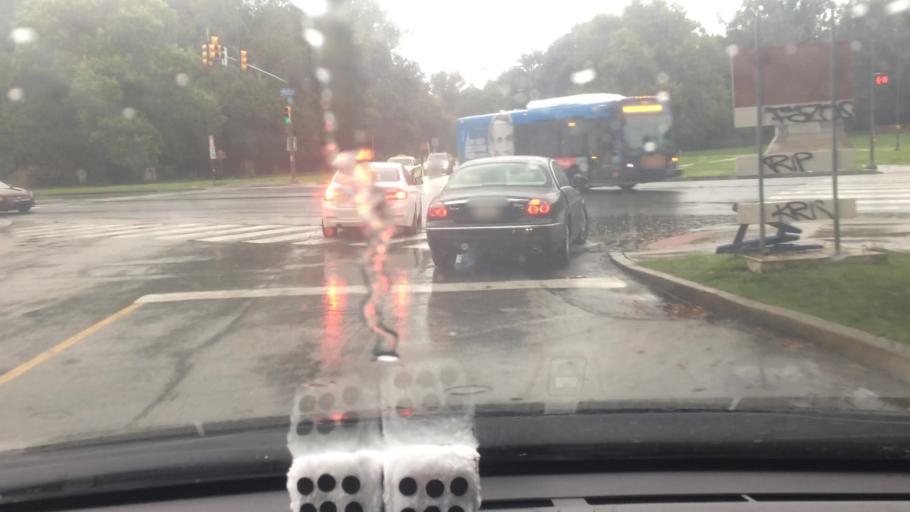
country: US
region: Pennsylvania
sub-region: Philadelphia County
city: Philadelphia
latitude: 39.9690
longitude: -75.1846
